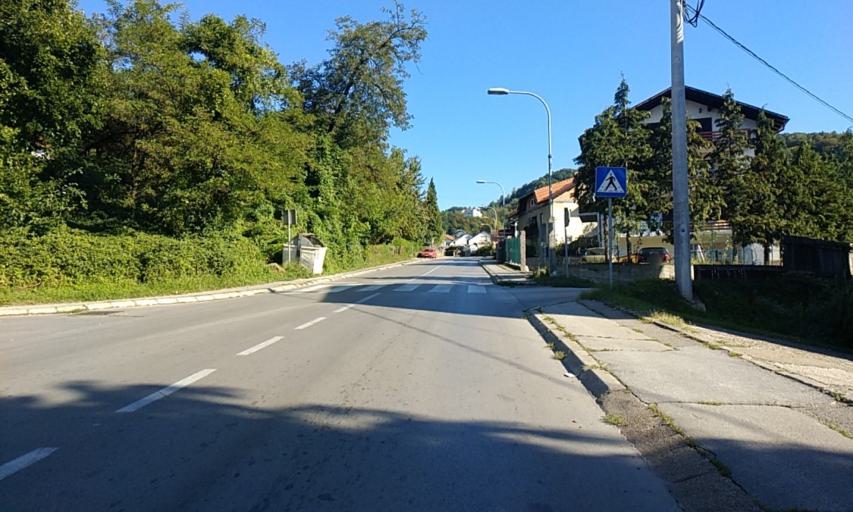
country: BA
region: Republika Srpska
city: Starcevica
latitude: 44.7575
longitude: 17.2071
